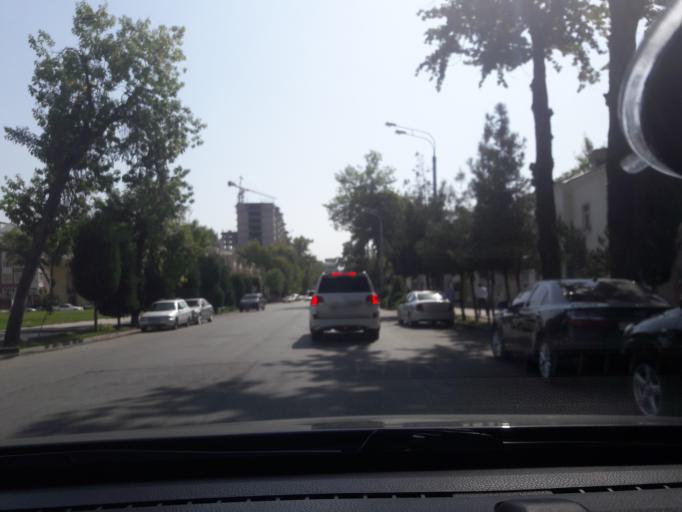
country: TJ
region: Dushanbe
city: Dushanbe
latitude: 38.5665
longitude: 68.7999
